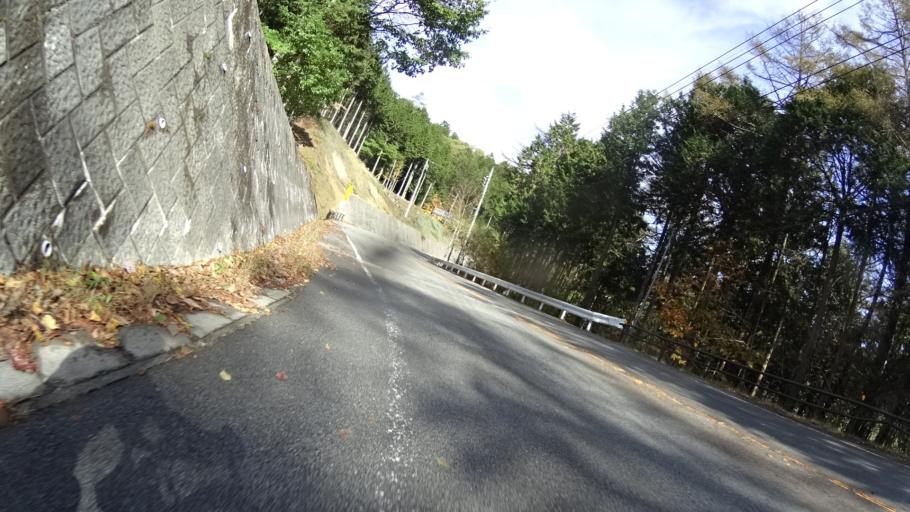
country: JP
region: Yamanashi
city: Enzan
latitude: 35.7909
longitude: 138.8042
